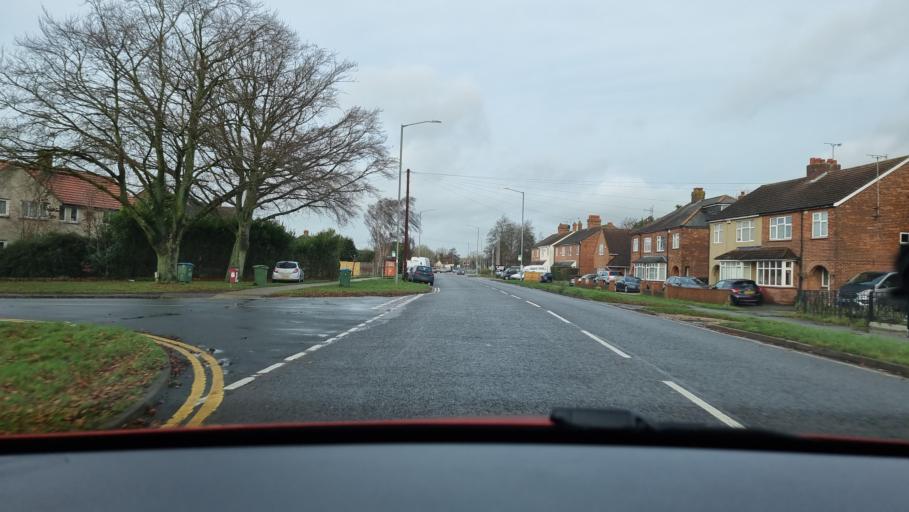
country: GB
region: England
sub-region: Buckinghamshire
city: Aylesbury
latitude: 51.8252
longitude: -0.8146
